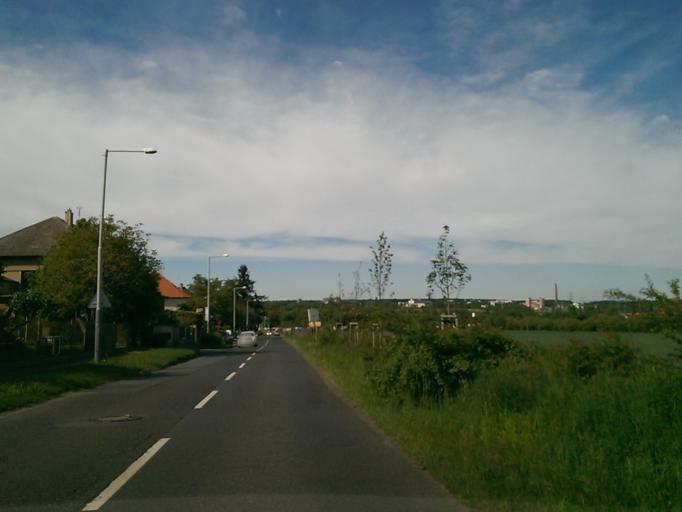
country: CZ
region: Praha
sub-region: Praha 14
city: Dolni Pocernice
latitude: 50.0771
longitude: 14.6034
